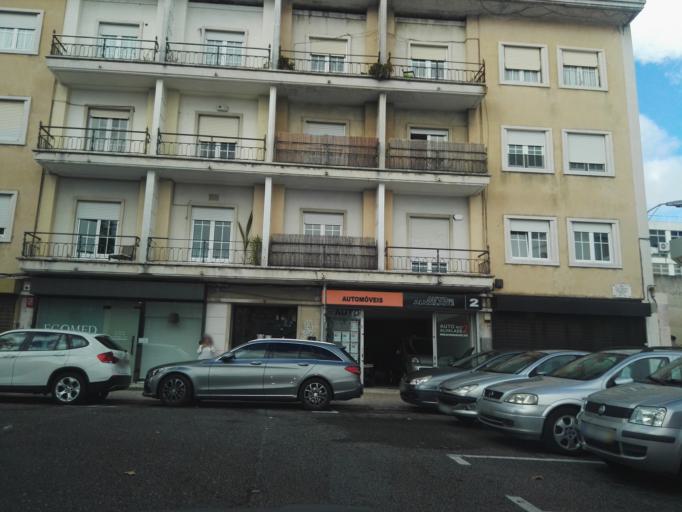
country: PT
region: Lisbon
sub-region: Lisbon
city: Lisbon
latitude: 38.7553
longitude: -9.1410
